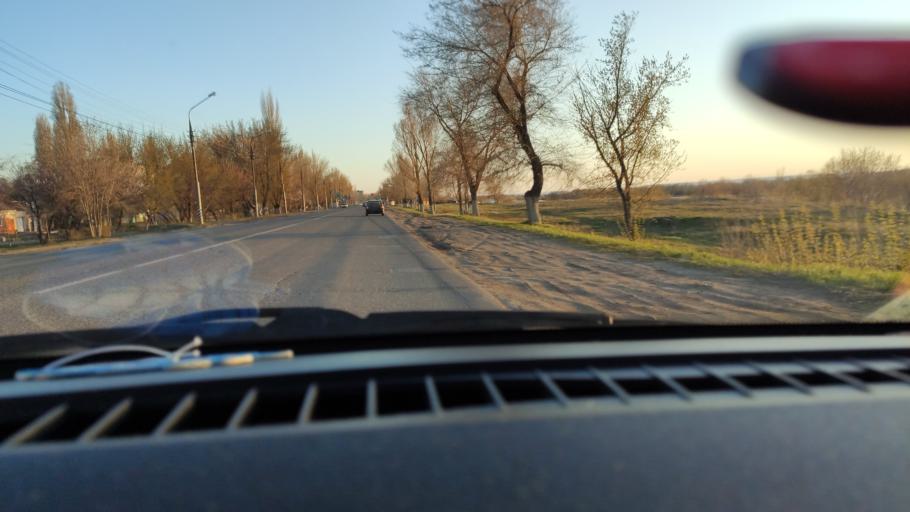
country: RU
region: Saratov
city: Engel's
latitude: 51.4553
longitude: 46.0864
